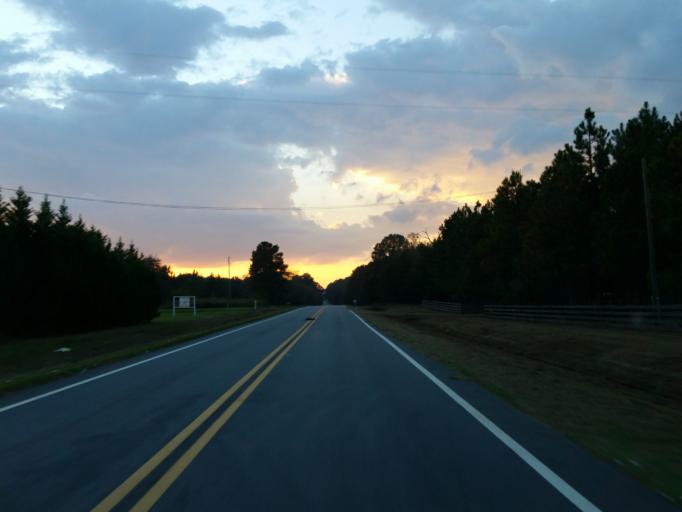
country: US
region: Georgia
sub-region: Pulaski County
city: Hawkinsville
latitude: 32.2079
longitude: -83.5396
